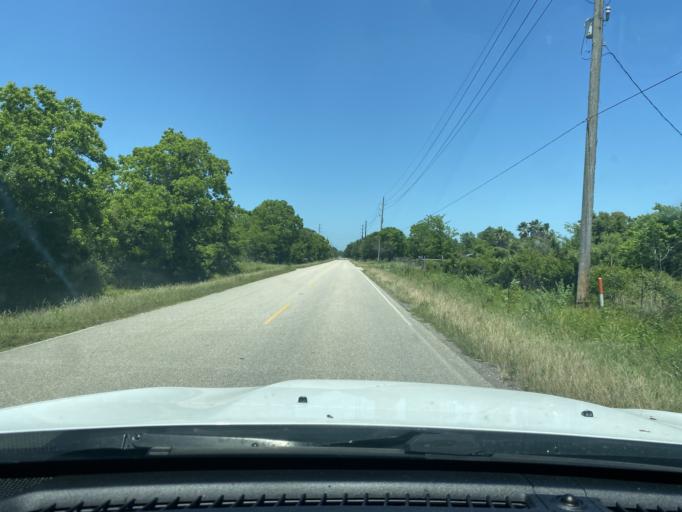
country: US
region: Texas
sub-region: Waller County
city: Waller
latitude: 30.0067
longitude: -95.8486
